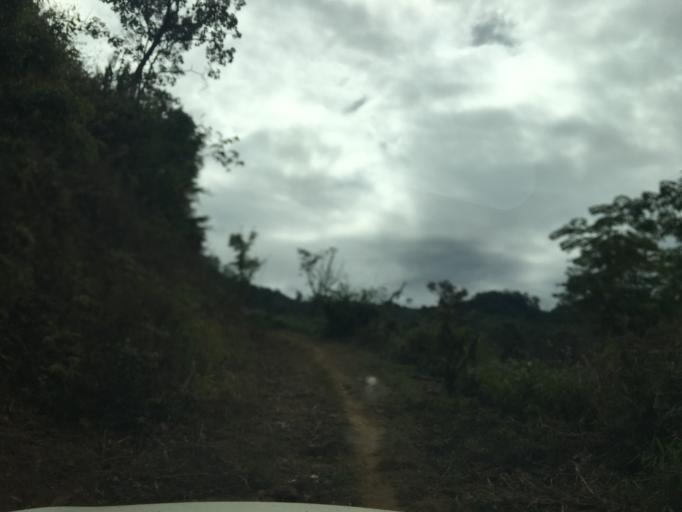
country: LA
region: Houaphan
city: Viengthong
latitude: 19.9210
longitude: 103.2967
